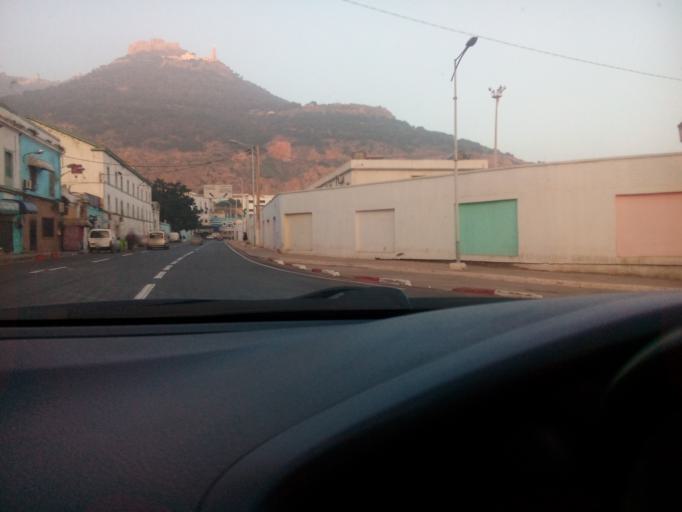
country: DZ
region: Oran
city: Oran
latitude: 35.7077
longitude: -0.6526
